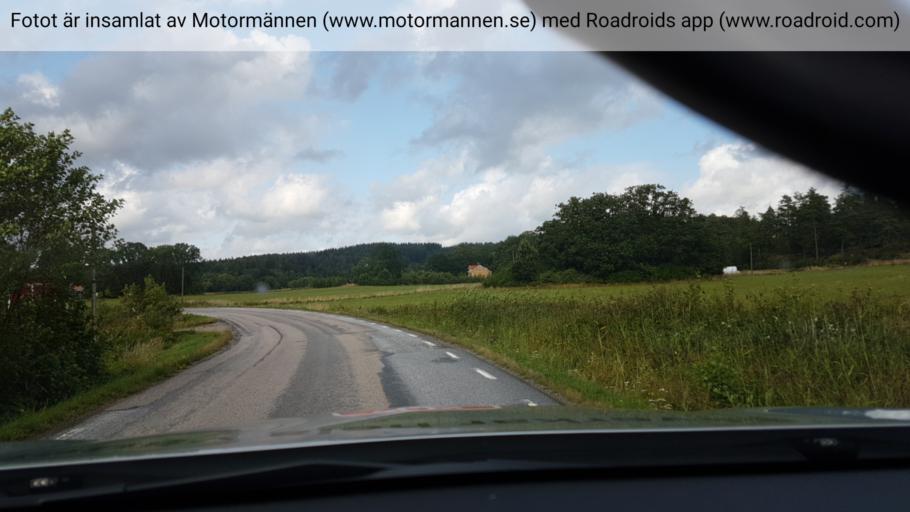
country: SE
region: Vaestra Goetaland
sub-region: Uddevalla Kommun
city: Ljungskile
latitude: 58.2487
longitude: 11.8633
